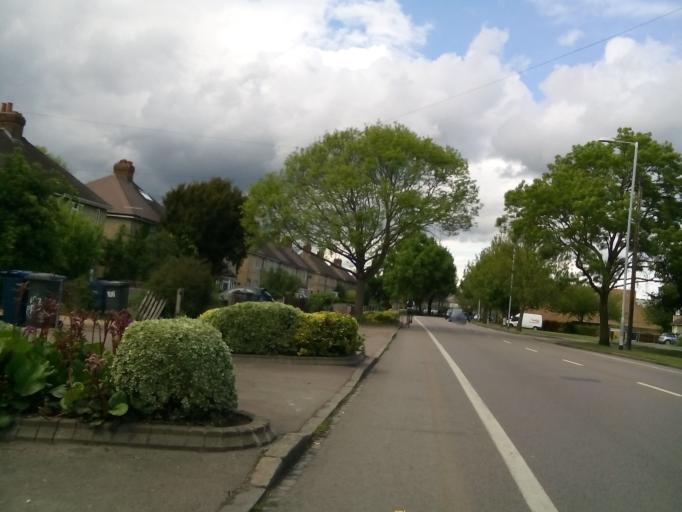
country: GB
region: England
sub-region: Cambridgeshire
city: Cambridge
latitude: 52.1973
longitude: 0.1562
